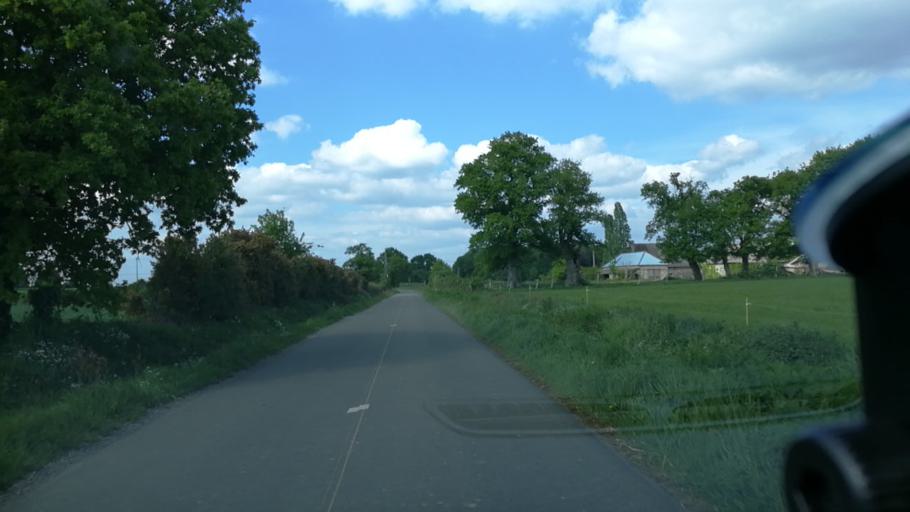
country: FR
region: Brittany
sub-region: Departement d'Ille-et-Vilaine
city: Martigne-Ferchaud
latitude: 47.8524
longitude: -1.3234
